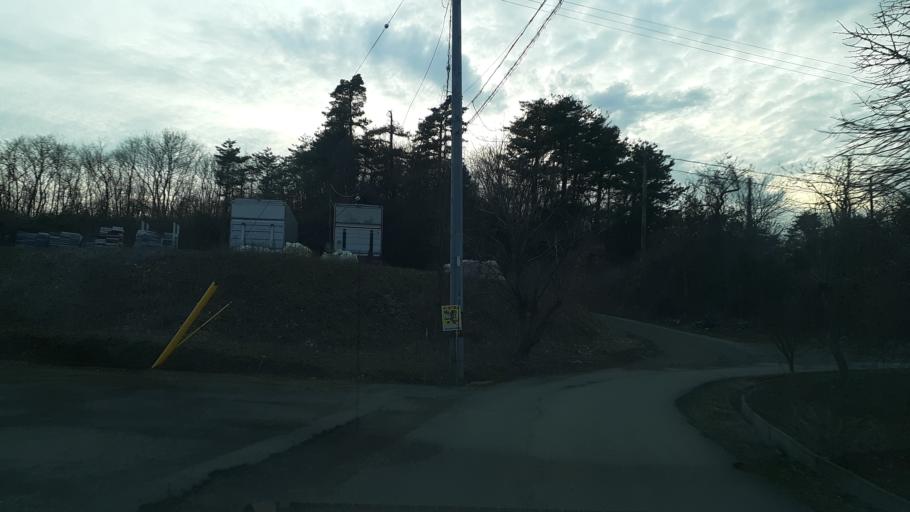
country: JP
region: Fukushima
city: Kitakata
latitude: 37.5341
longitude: 139.9493
